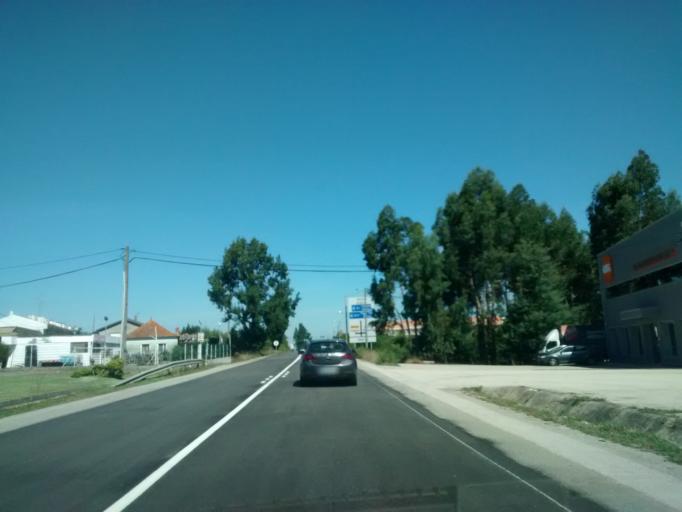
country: PT
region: Aveiro
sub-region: Oliveira do Bairro
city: Oia
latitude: 40.5407
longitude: -8.5308
